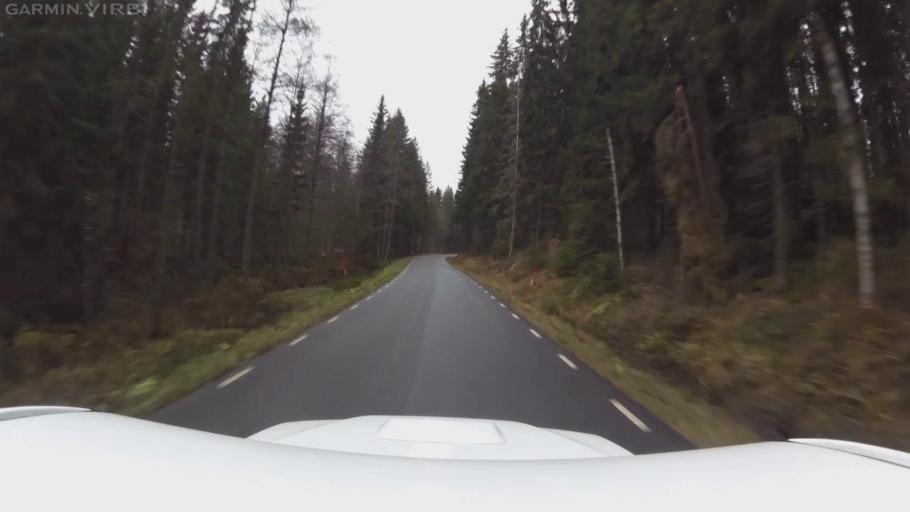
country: SE
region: OEstergoetland
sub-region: Mjolby Kommun
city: Mantorp
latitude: 58.1699
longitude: 15.3975
